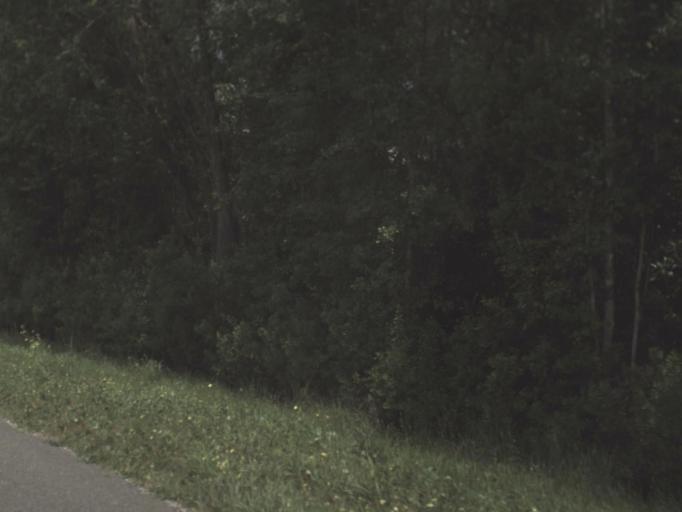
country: US
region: Florida
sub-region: Columbia County
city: Five Points
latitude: 30.2779
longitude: -82.6310
